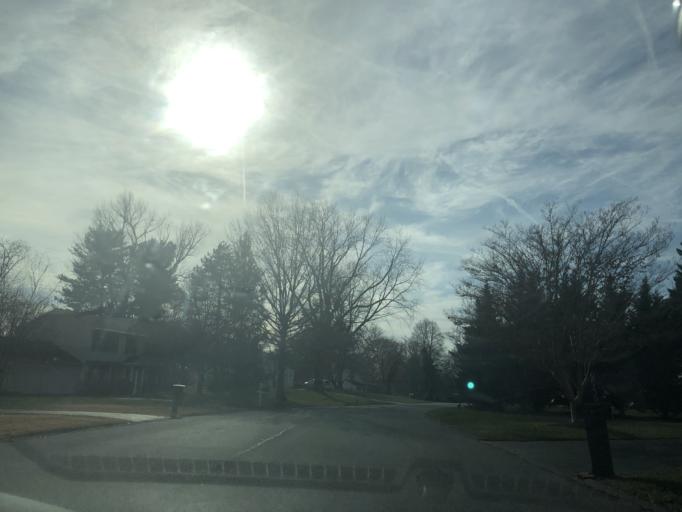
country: US
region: Maryland
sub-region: Howard County
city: Columbia
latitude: 39.2850
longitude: -76.8472
